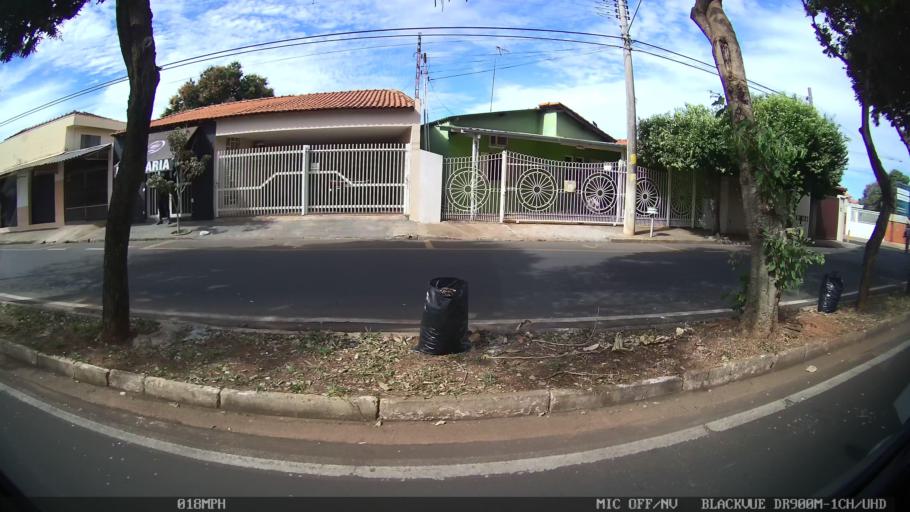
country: BR
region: Sao Paulo
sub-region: Catanduva
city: Catanduva
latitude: -21.1311
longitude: -48.9561
